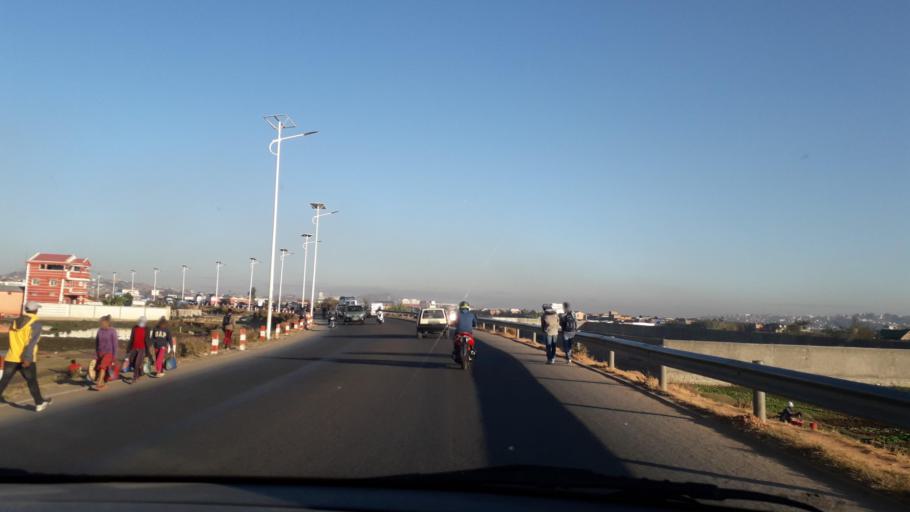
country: MG
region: Analamanga
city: Antananarivo
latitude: -18.8942
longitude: 47.5086
